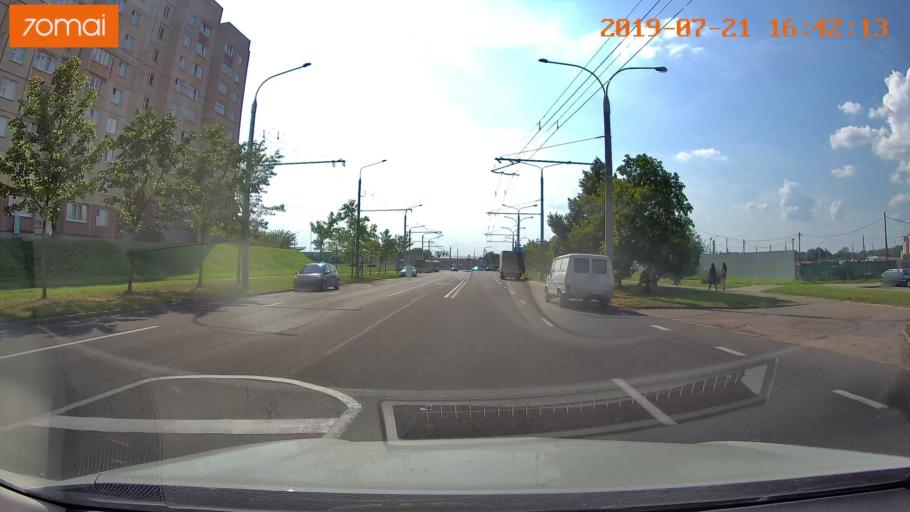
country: BY
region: Minsk
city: Novoye Medvezhino
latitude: 53.9013
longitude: 27.4263
